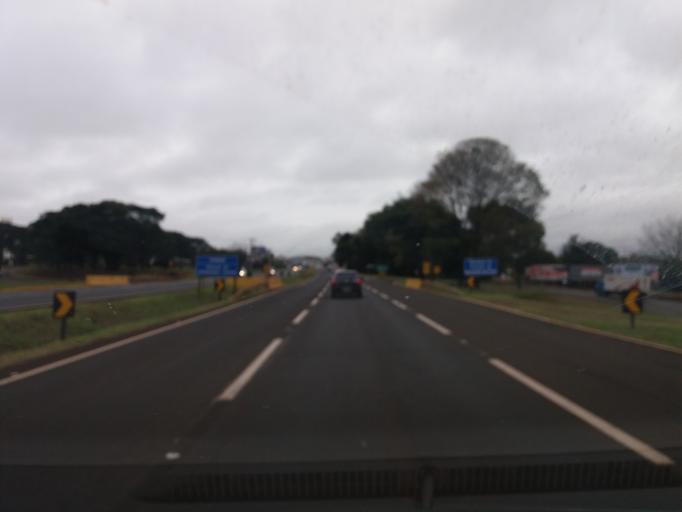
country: BR
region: Parana
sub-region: Paicandu
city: Paicandu
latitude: -23.4711
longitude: -51.9968
